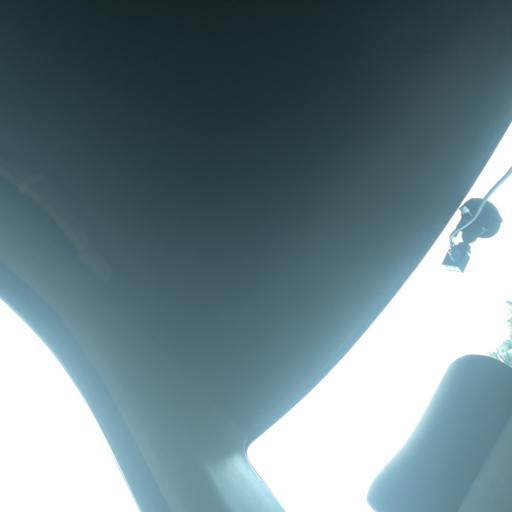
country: NG
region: Lagos
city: Ejirin
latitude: 6.6455
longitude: 3.7247
